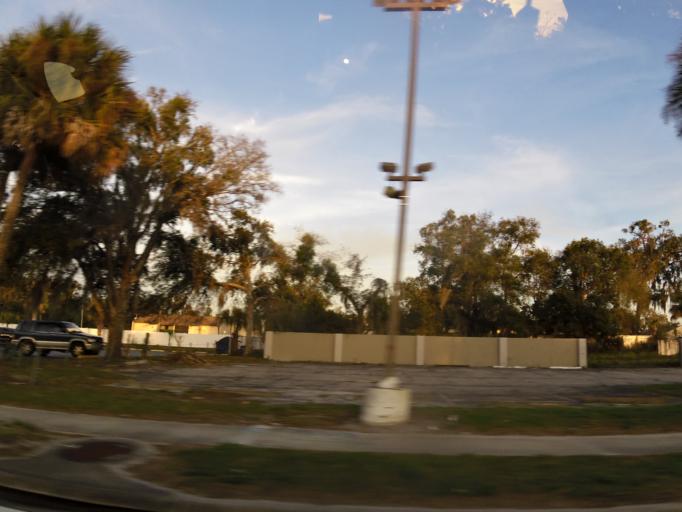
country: US
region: Florida
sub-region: Volusia County
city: North DeLand
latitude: 29.0493
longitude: -81.3040
